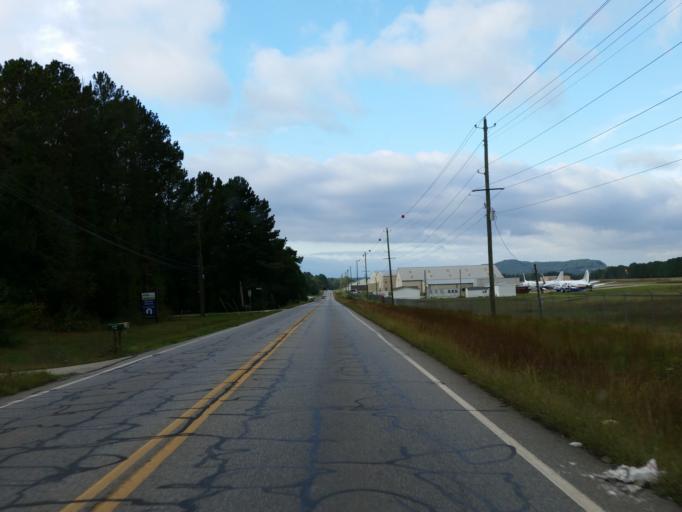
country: US
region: Georgia
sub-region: Bartow County
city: Cartersville
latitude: 34.1155
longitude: -84.8512
